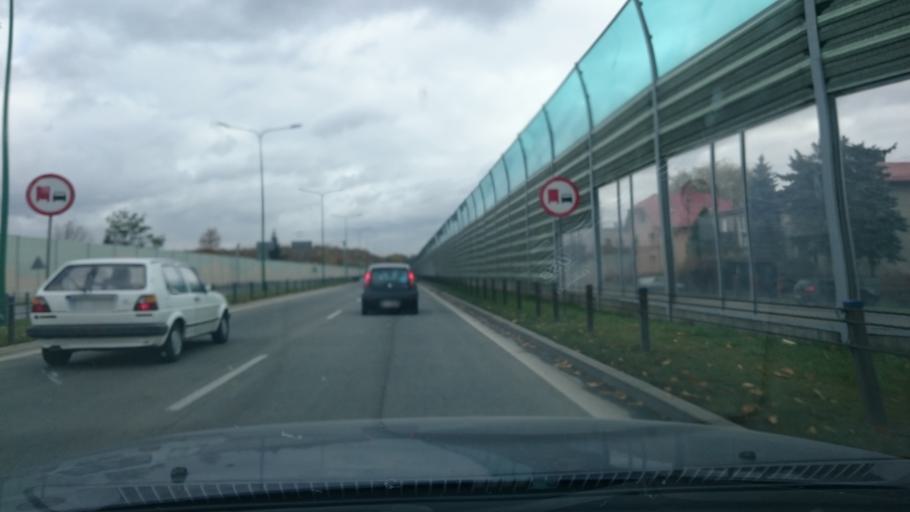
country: PL
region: Silesian Voivodeship
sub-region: Dabrowa Gornicza
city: Dabrowa Gornicza
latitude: 50.3171
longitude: 19.2179
